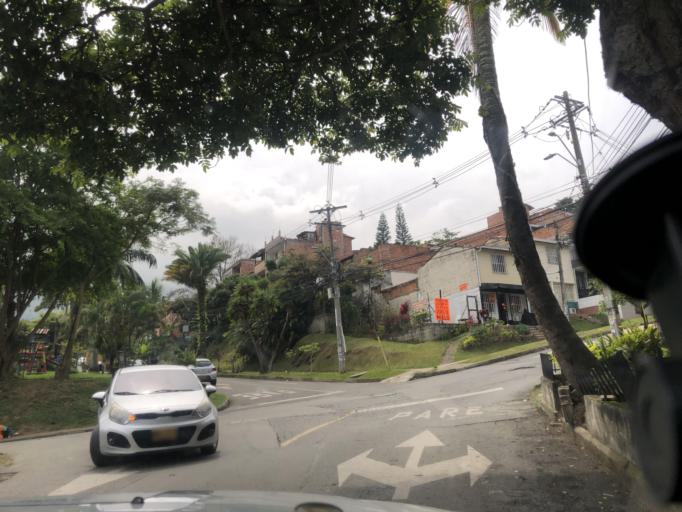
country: CO
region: Antioquia
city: Bello
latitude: 6.3313
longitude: -75.5380
